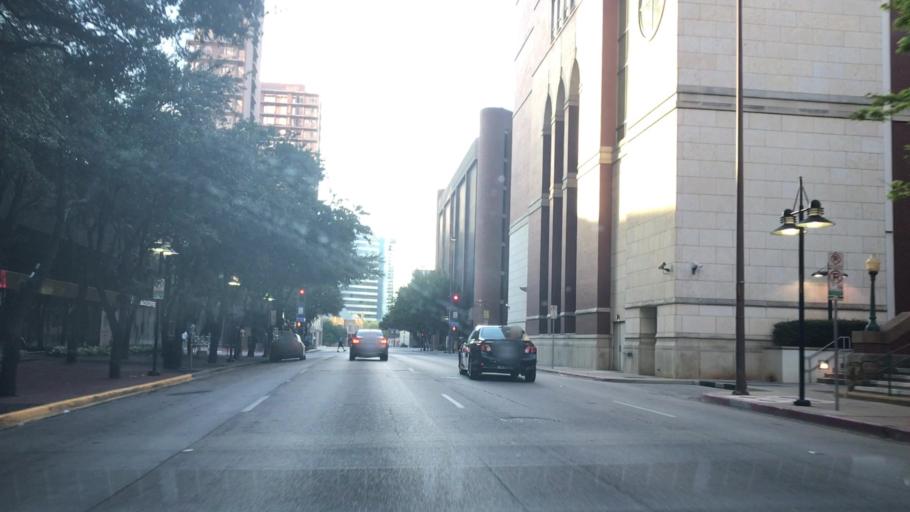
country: US
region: Texas
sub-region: Dallas County
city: Dallas
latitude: 32.7845
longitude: -96.7998
